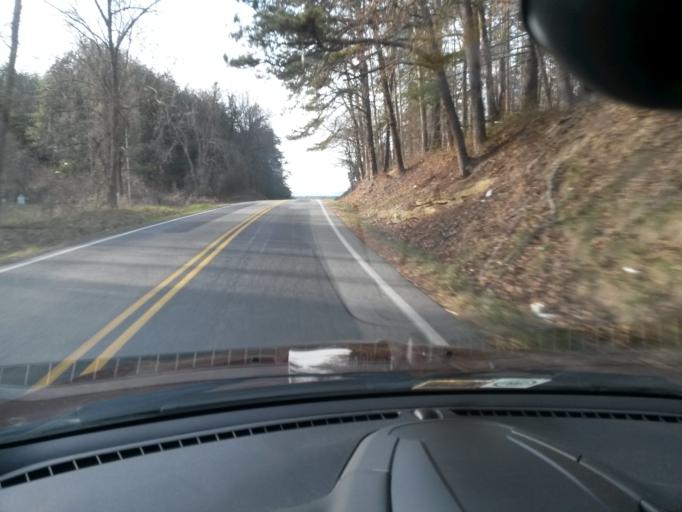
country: US
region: Virginia
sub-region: Bath County
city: Warm Springs
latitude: 37.9980
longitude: -79.5608
